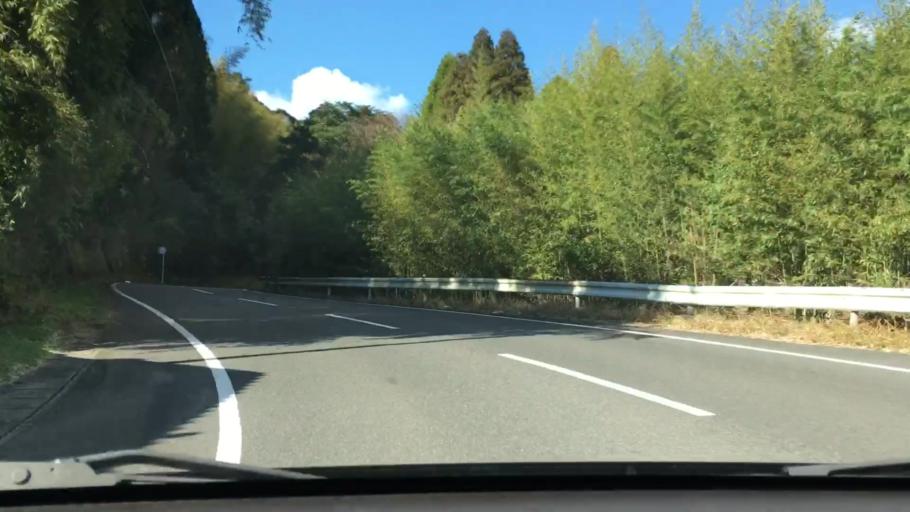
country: JP
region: Kagoshima
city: Ijuin
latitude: 31.7159
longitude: 130.4336
